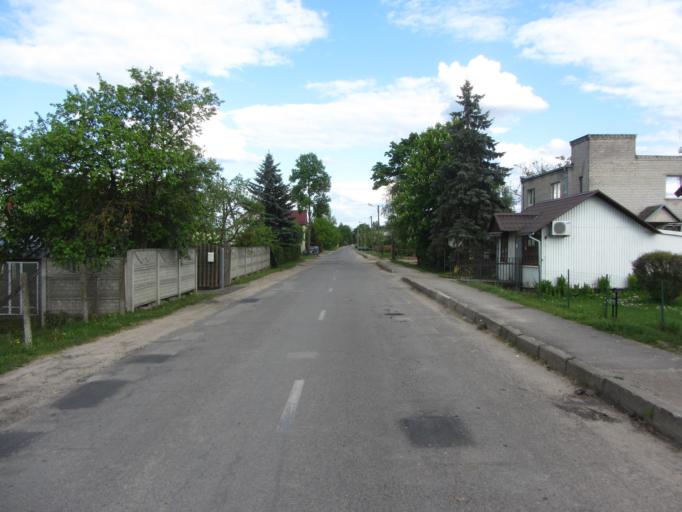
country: LT
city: Sirvintos
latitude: 55.0505
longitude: 24.9409
